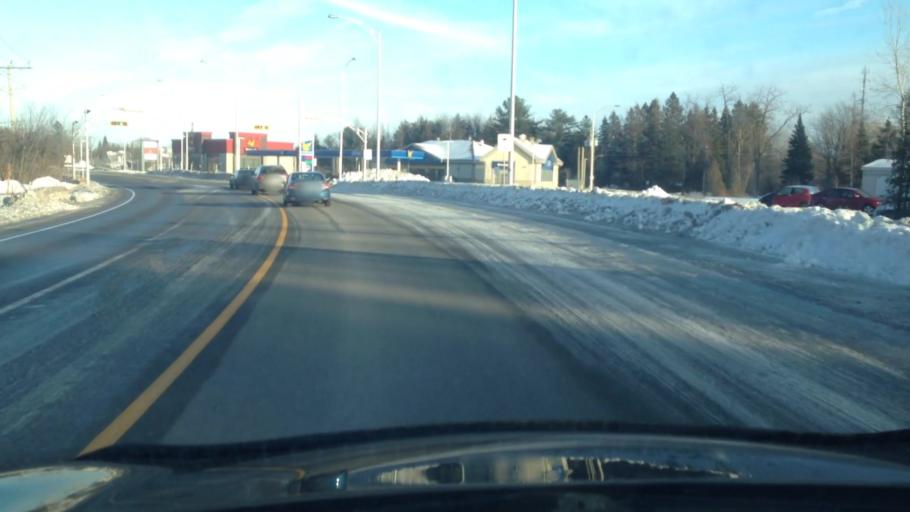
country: CA
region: Quebec
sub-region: Laurentides
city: Sainte-Sophie
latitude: 45.8160
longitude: -73.9067
